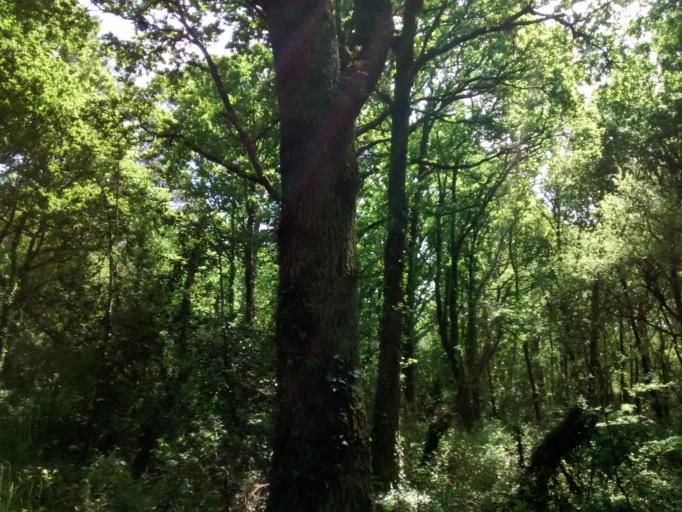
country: FR
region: Brittany
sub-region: Departement du Morbihan
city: Larmor-Baden
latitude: 47.6002
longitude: -2.9010
